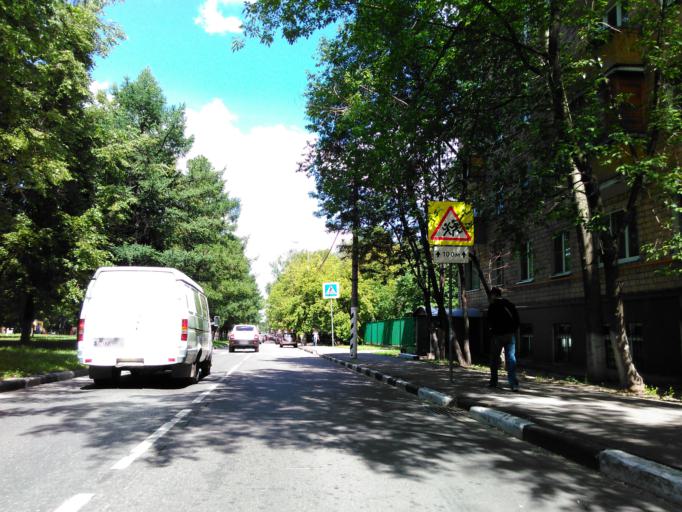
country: RU
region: Moscow
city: Novyye Cheremushki
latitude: 55.6891
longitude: 37.5875
